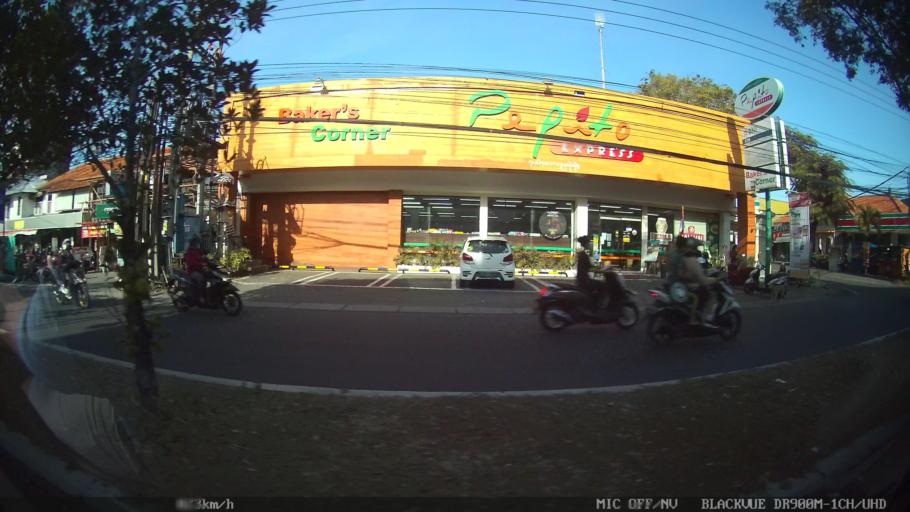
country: ID
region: Bali
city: Jimbaran
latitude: -8.7857
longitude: 115.1877
